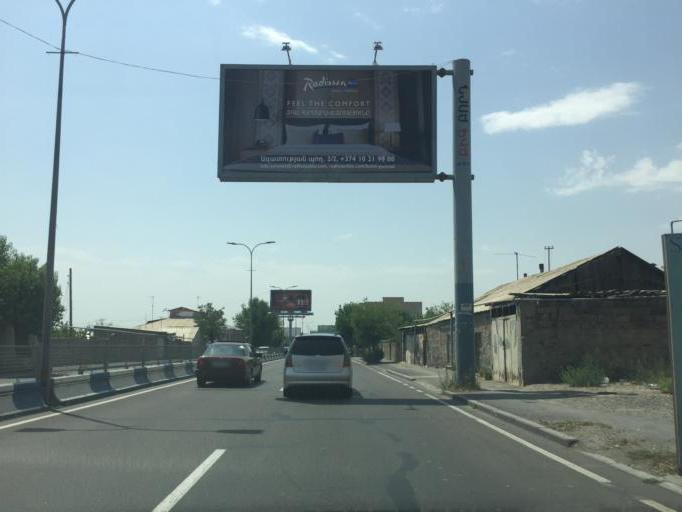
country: AM
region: Armavir
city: Mertsavan
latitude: 40.1645
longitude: 44.4132
